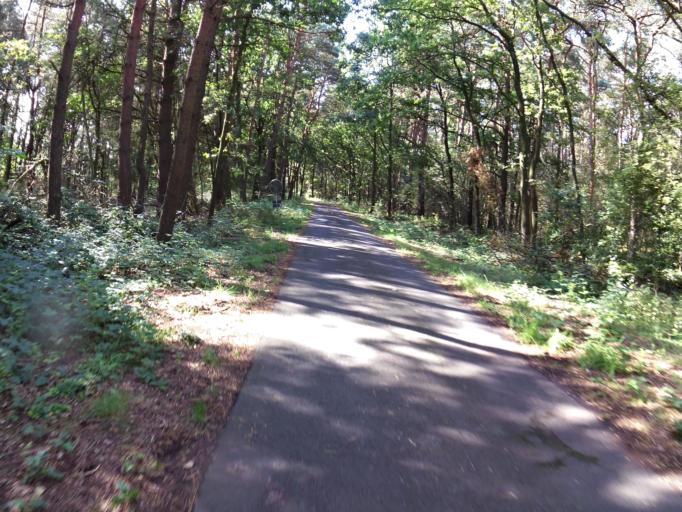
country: DE
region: Lower Saxony
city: Sandbostel
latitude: 53.3958
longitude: 9.1214
